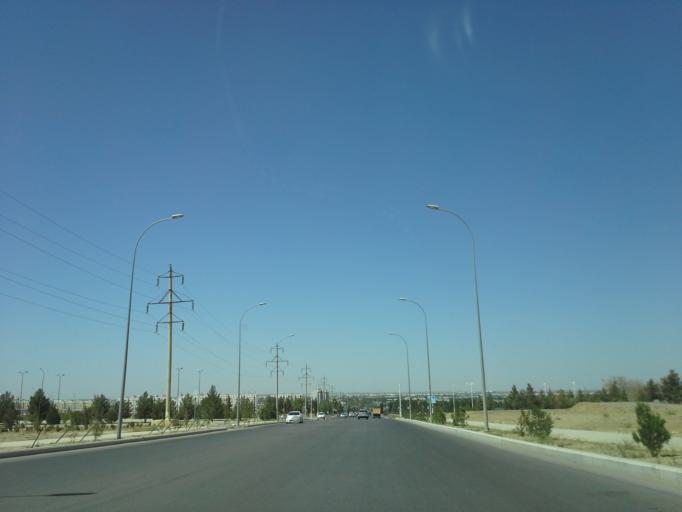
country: TM
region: Ahal
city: Ashgabat
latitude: 37.8982
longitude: 58.4057
